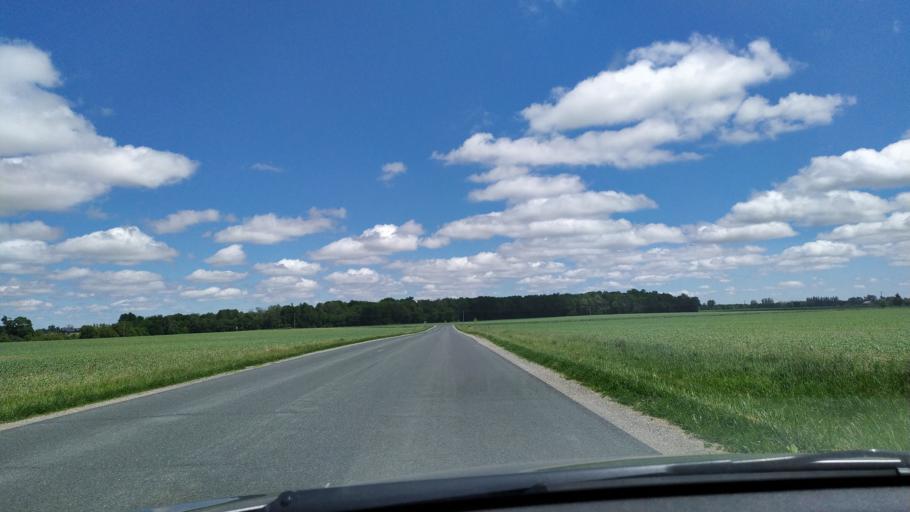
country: CA
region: Ontario
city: Huron East
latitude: 43.4524
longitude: -81.1866
